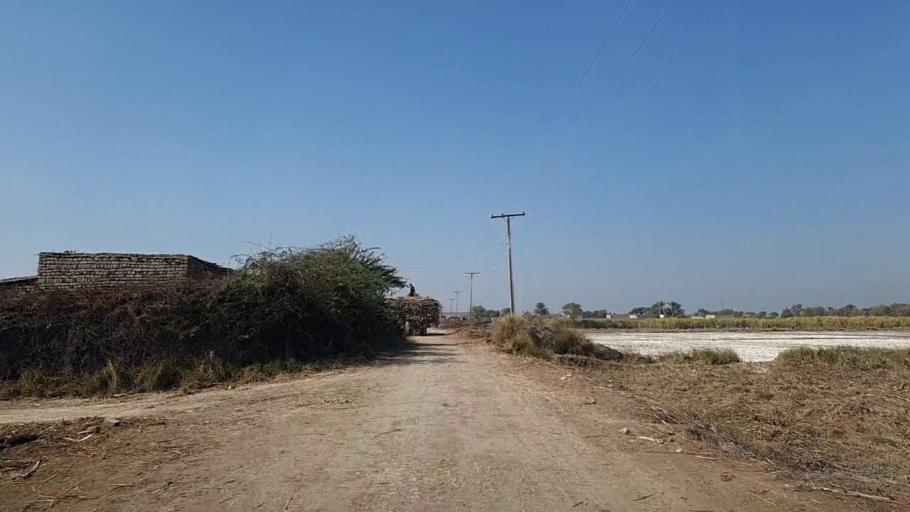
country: PK
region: Sindh
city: Nawabshah
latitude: 26.2870
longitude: 68.3755
